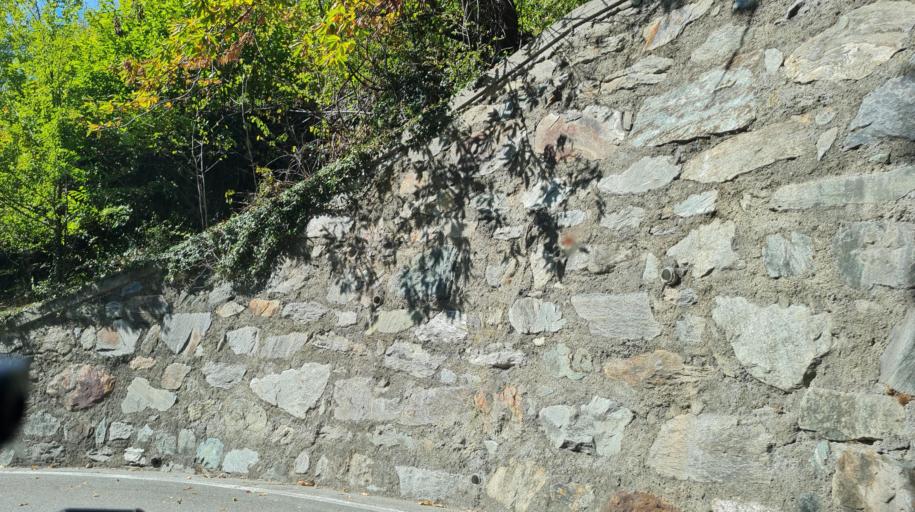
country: IT
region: Aosta Valley
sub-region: Valle d'Aosta
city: Arnad
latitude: 45.6414
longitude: 7.7356
